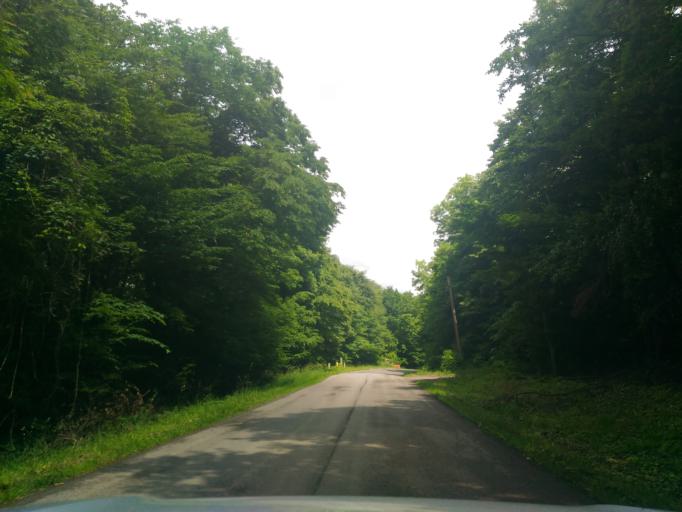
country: HU
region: Baranya
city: Pecs
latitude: 46.1285
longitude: 18.2283
